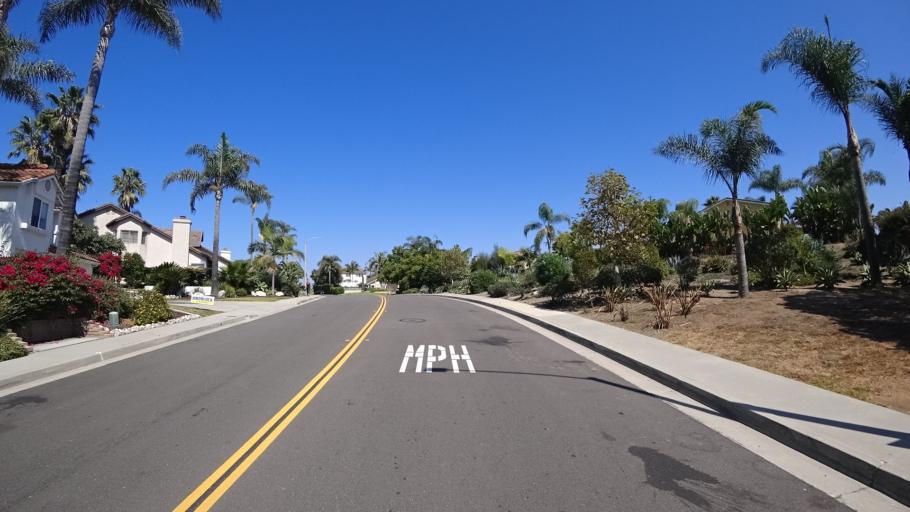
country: US
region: California
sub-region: Orange County
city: San Clemente
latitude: 33.4589
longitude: -117.6264
